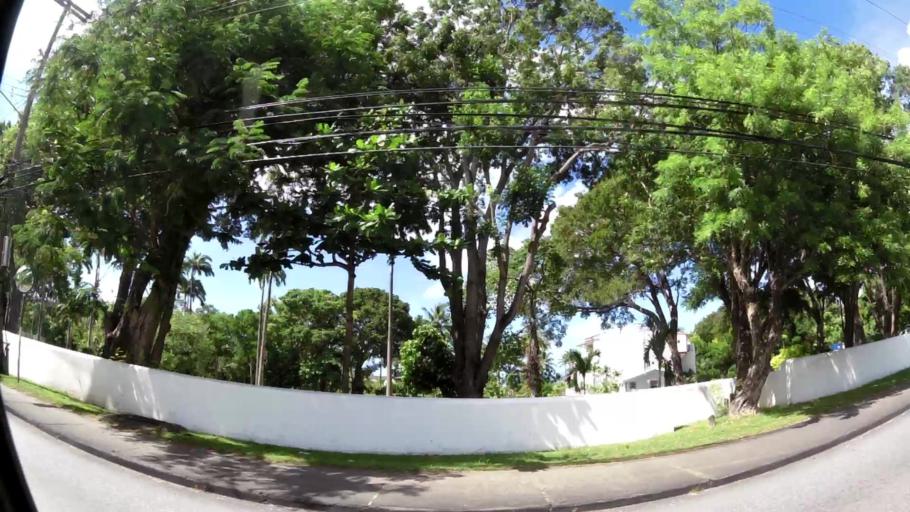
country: BB
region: Saint James
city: Holetown
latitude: 13.2004
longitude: -59.6396
